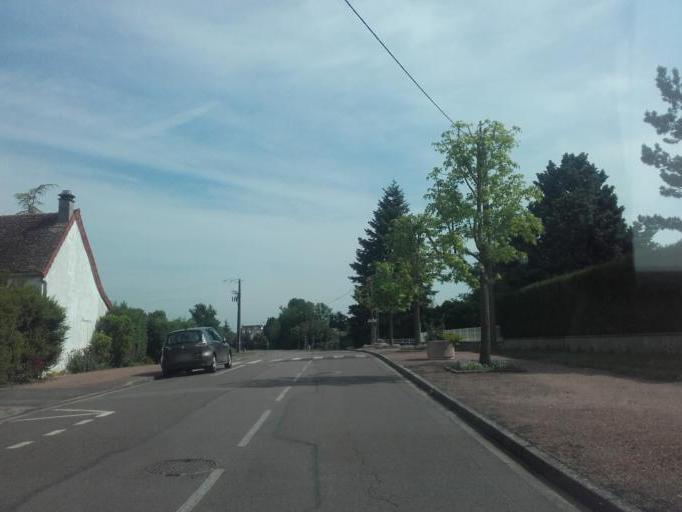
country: FR
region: Bourgogne
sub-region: Departement de la Cote-d'Or
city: Corpeau
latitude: 46.9318
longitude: 4.7539
